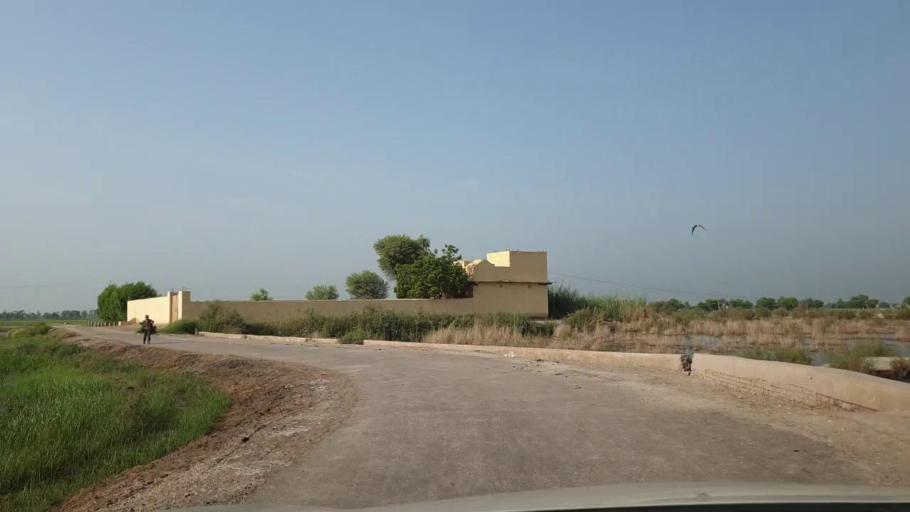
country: PK
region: Sindh
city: Larkana
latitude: 27.4914
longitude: 68.2118
